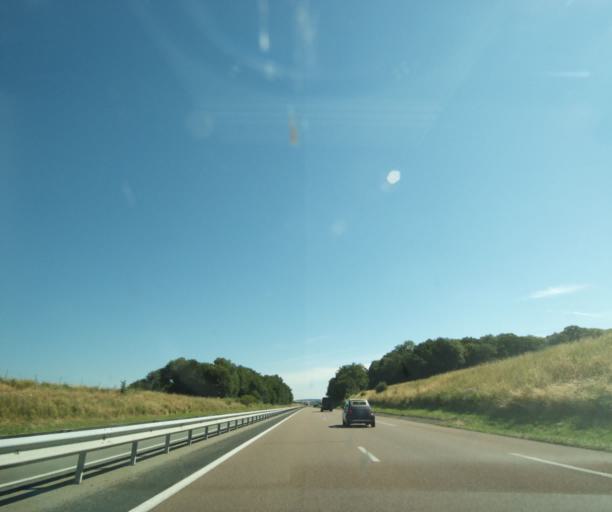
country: FR
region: Champagne-Ardenne
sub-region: Departement de la Haute-Marne
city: Saulxures
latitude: 48.0691
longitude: 5.5937
